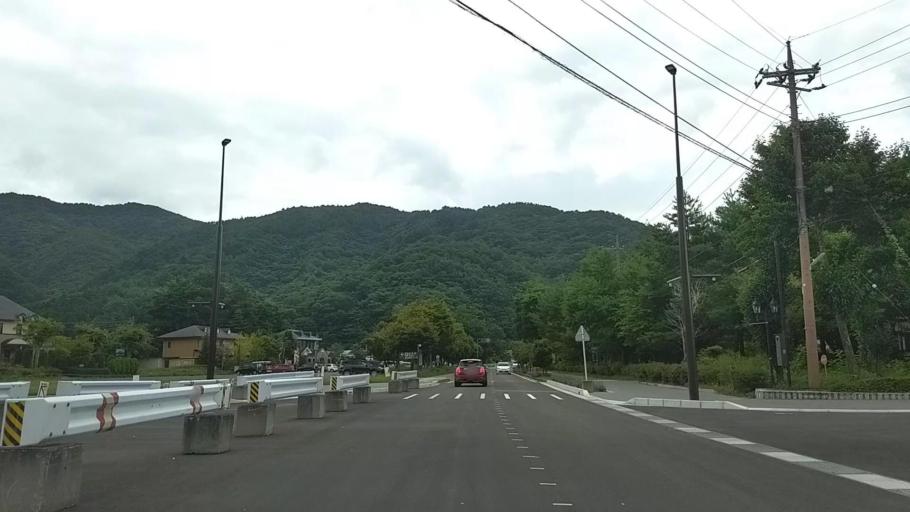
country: JP
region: Yamanashi
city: Fujikawaguchiko
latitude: 35.5216
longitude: 138.7702
